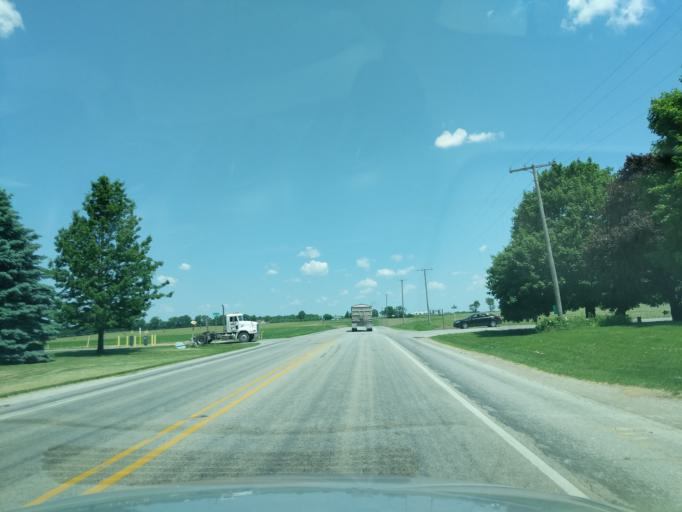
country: US
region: Indiana
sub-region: Noble County
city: Ligonier
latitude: 41.4809
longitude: -85.5774
